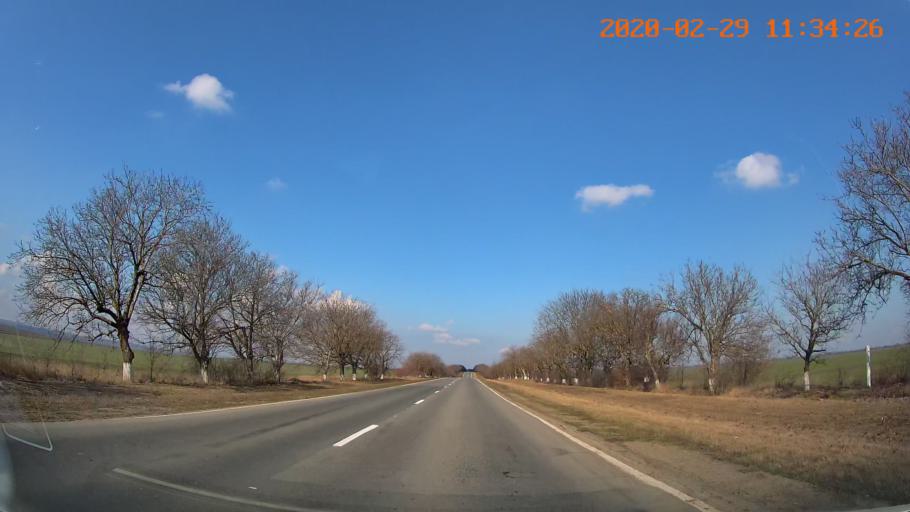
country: MD
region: Rezina
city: Saharna
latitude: 47.5658
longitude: 29.0737
